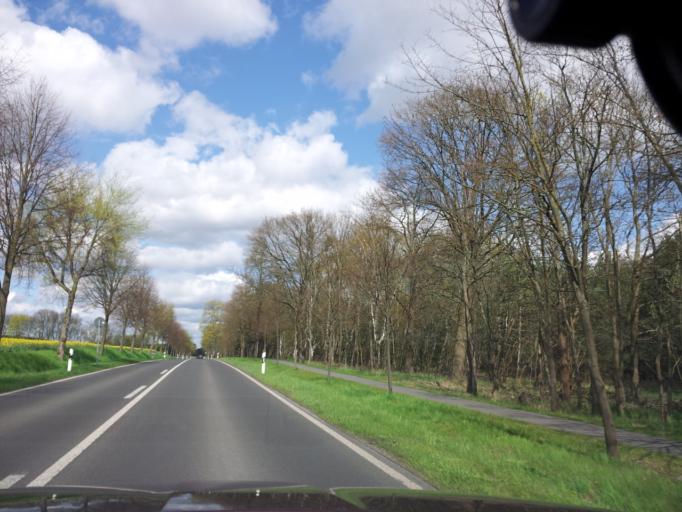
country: DE
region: Brandenburg
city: Bernau bei Berlin
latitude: 52.6958
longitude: 13.6061
